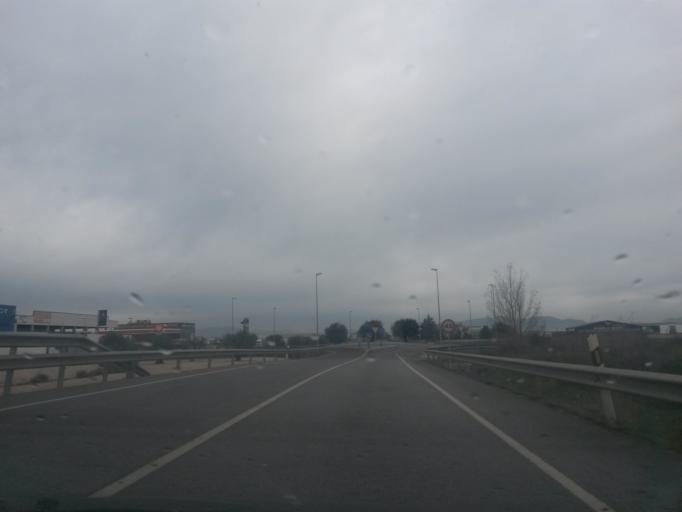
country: ES
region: Catalonia
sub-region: Provincia de Girona
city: Vilamalla
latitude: 42.2284
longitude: 2.9550
